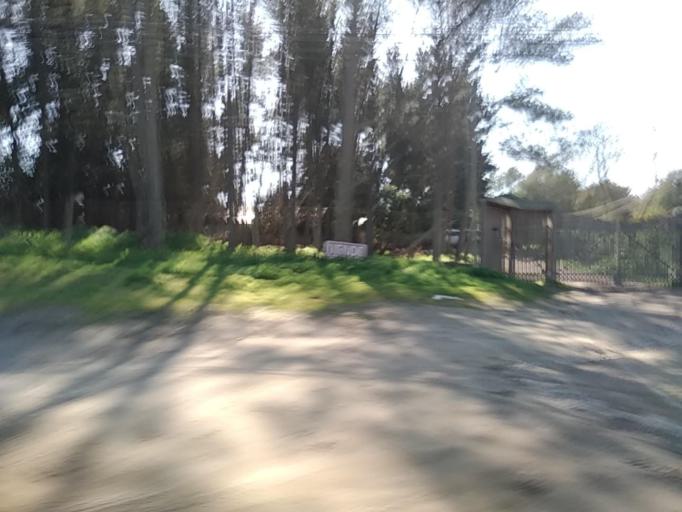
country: CL
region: Valparaiso
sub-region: Provincia de Valparaiso
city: Vina del Mar
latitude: -32.9595
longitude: -71.5333
